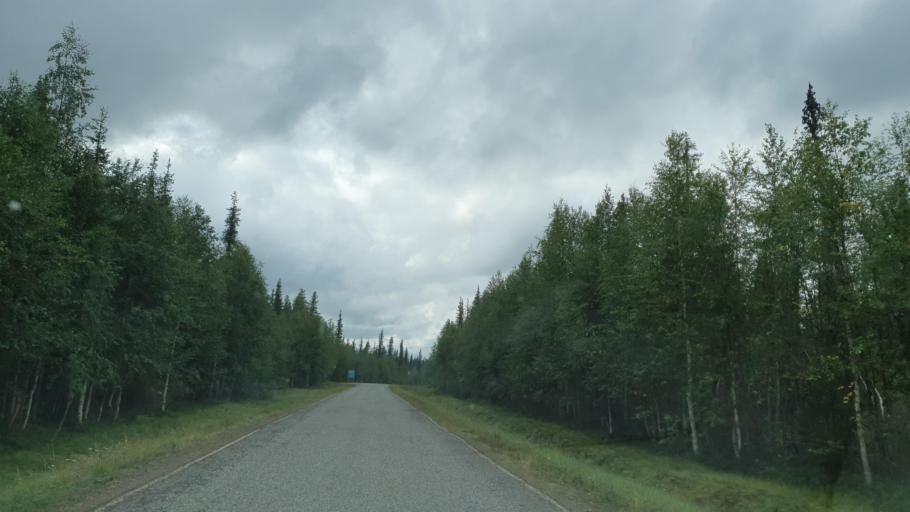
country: FI
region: Lapland
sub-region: Tunturi-Lappi
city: Muonio
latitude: 67.7206
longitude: 24.2276
